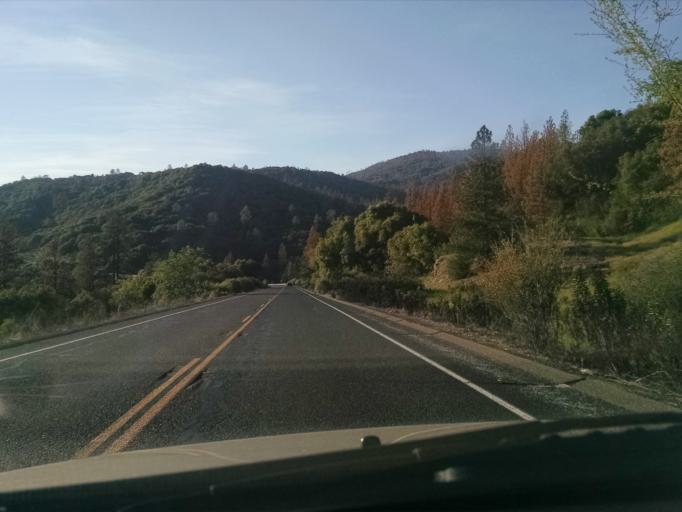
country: US
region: California
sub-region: Madera County
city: Ahwahnee
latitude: 37.4427
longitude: -119.7426
